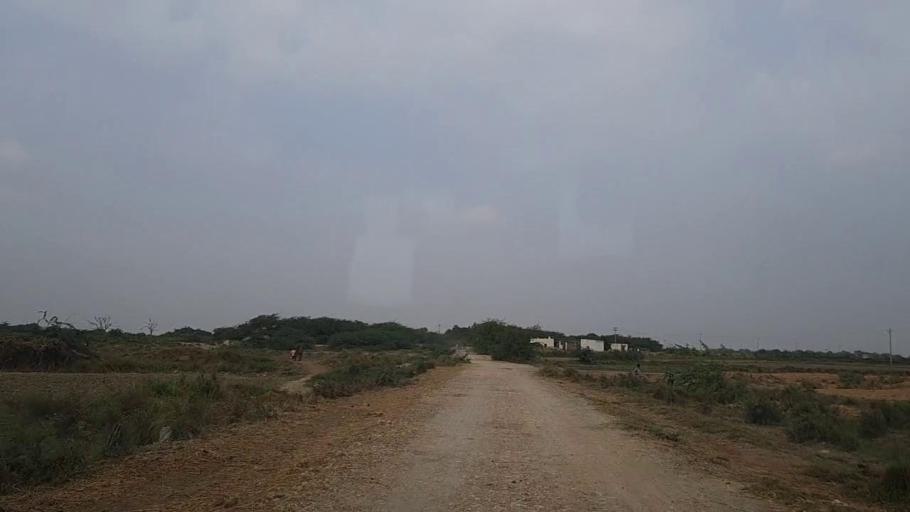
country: PK
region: Sindh
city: Mirpur Sakro
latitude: 24.6012
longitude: 67.6983
